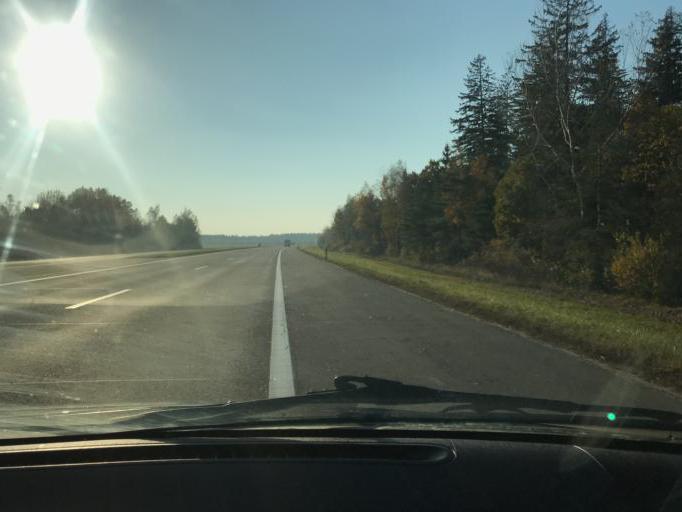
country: BY
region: Minsk
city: Krupki
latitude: 54.3149
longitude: 29.0448
